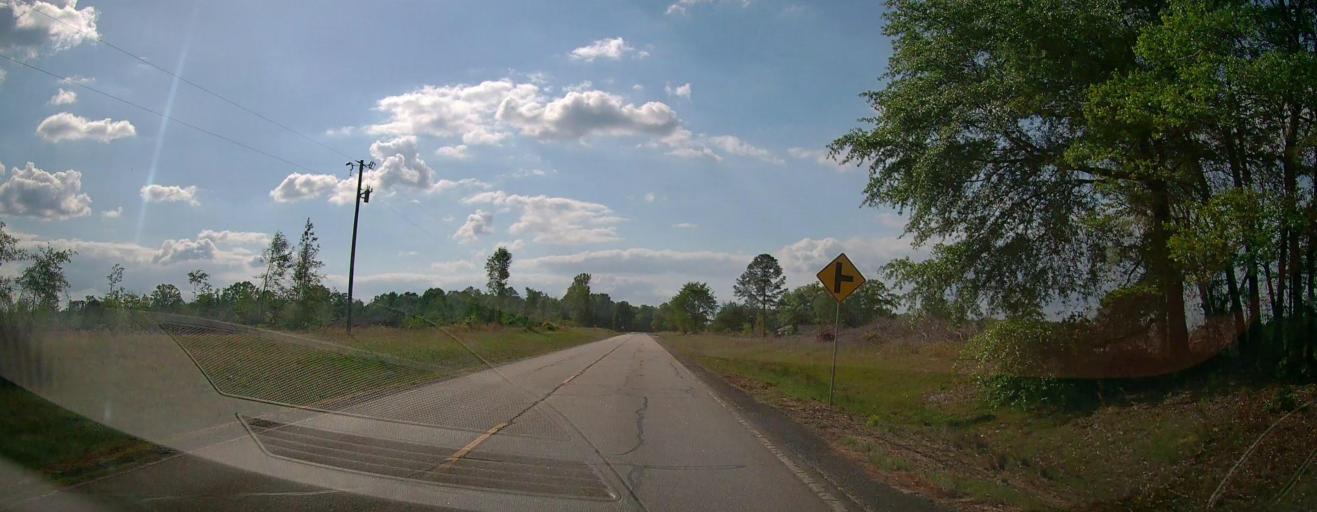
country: US
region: Georgia
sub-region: Washington County
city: Tennille
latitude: 32.9100
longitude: -82.9799
